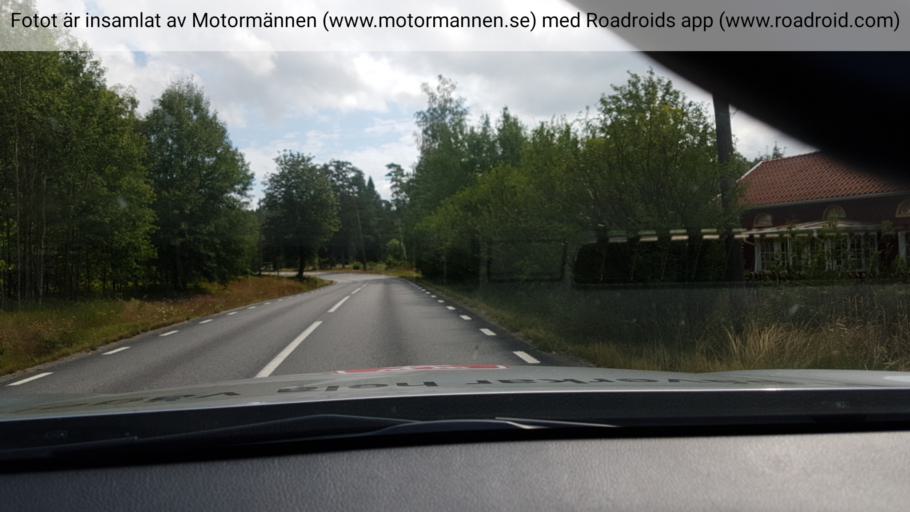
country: SE
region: Vaestra Goetaland
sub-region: Svenljunga Kommun
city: Svenljunga
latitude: 57.4650
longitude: 13.2011
